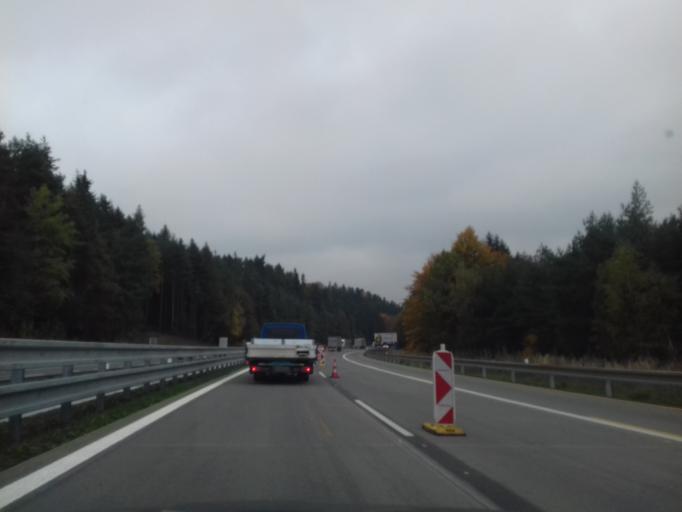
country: CZ
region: Central Bohemia
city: Ondrejov
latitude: 49.8469
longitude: 14.7976
